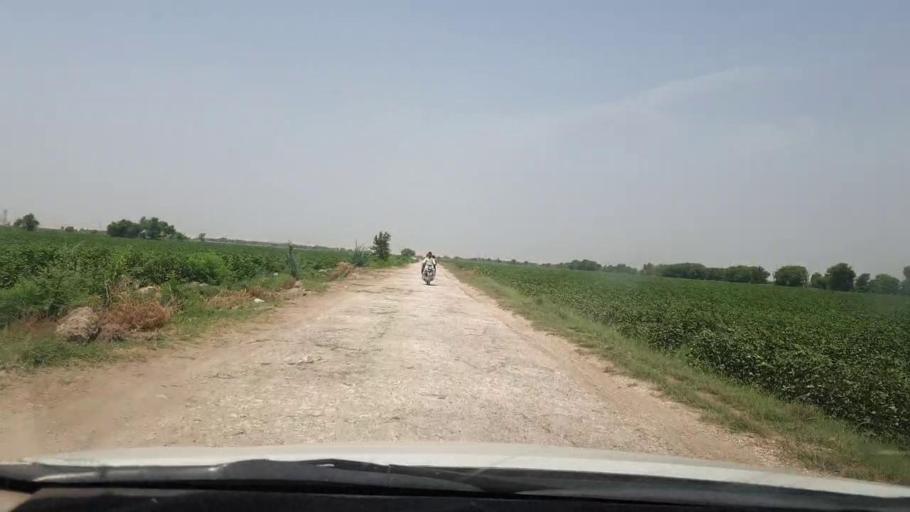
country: PK
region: Sindh
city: Rohri
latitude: 27.4974
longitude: 69.0194
